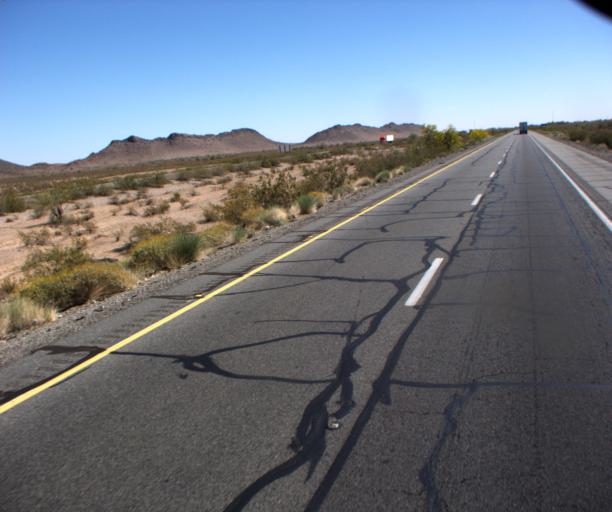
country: US
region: Arizona
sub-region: Maricopa County
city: Buckeye
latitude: 33.5231
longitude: -113.0862
